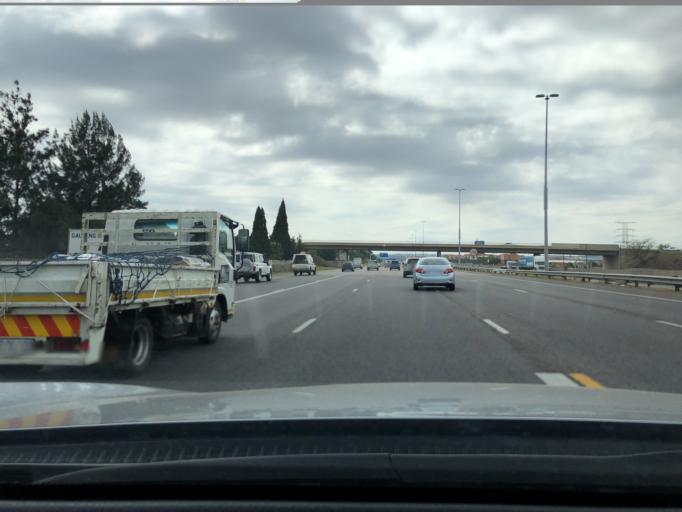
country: ZA
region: Gauteng
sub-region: City of Tshwane Metropolitan Municipality
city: Centurion
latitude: -25.8749
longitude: 28.1751
